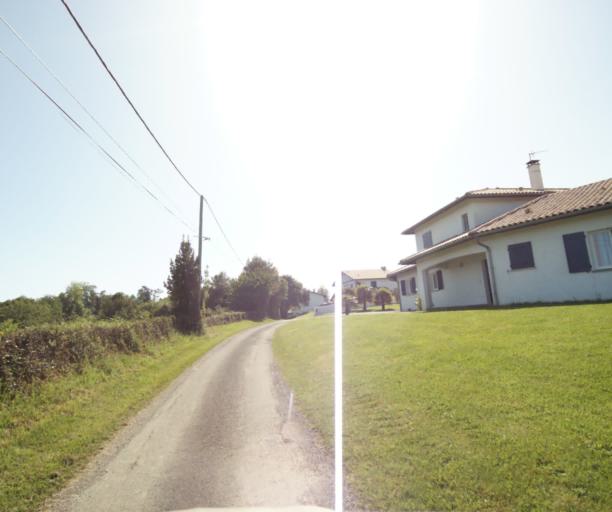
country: FR
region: Aquitaine
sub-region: Departement des Pyrenees-Atlantiques
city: Villefranque
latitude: 43.4528
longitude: -1.4469
